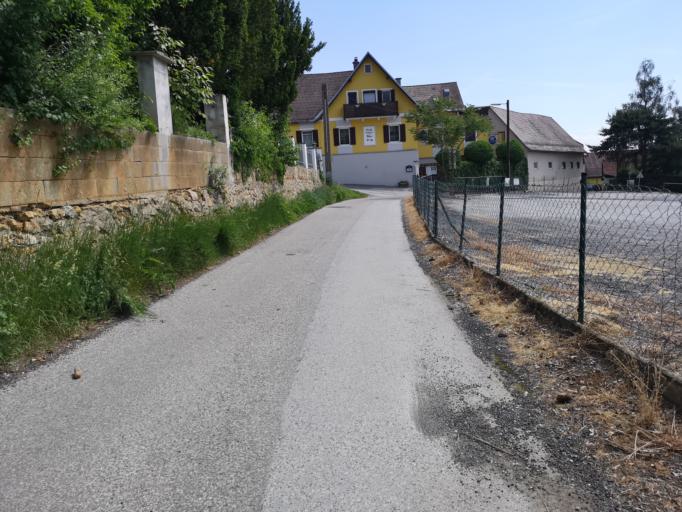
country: AT
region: Styria
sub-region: Graz Stadt
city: Wetzelsdorf
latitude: 47.0323
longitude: 15.3799
